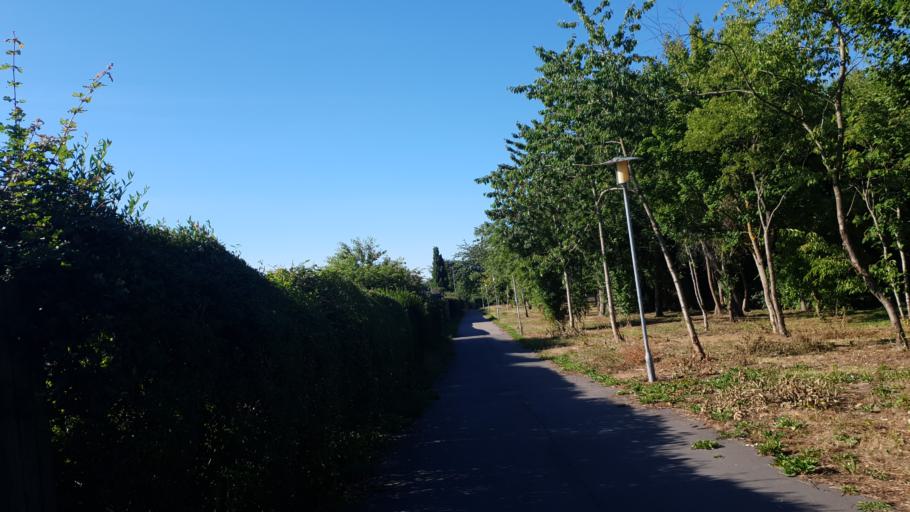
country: DK
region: South Denmark
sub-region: Fredericia Kommune
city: Fredericia
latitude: 55.5642
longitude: 9.7215
